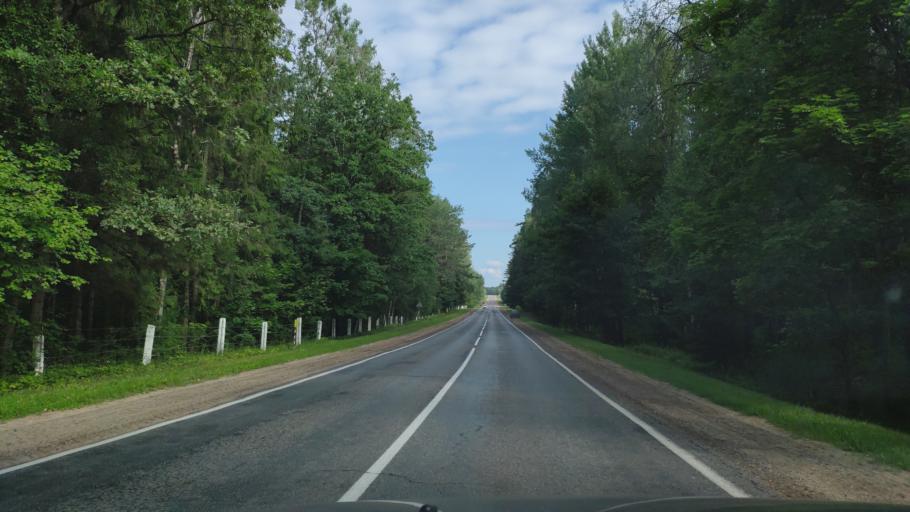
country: BY
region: Minsk
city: Novosel'ye
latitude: 53.9526
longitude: 27.2459
